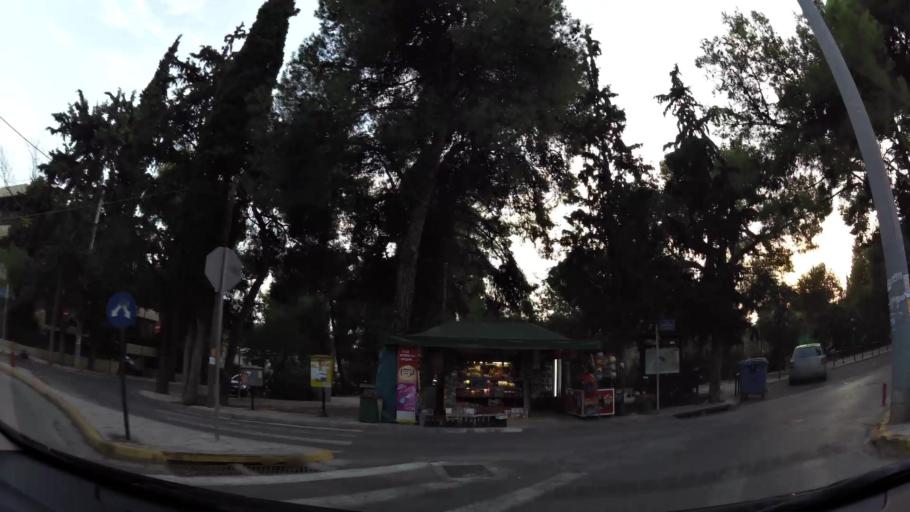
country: GR
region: Attica
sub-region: Nomarchia Athinas
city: Psychiko
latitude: 38.0138
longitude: 23.7785
